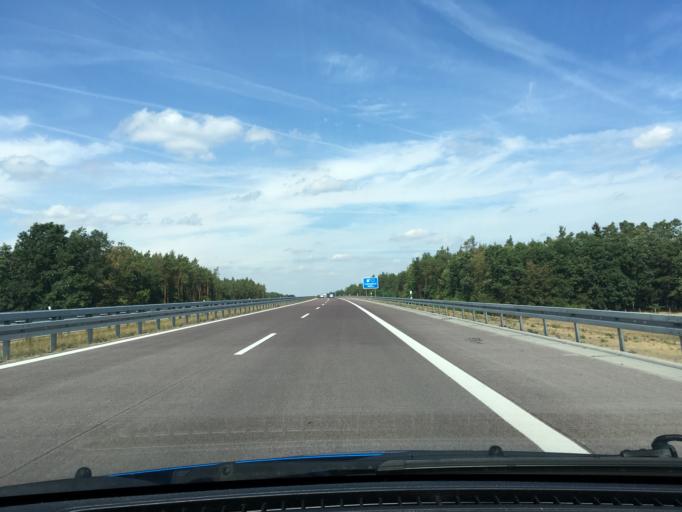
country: DE
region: Mecklenburg-Vorpommern
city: Gross Laasch
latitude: 53.3330
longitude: 11.5255
